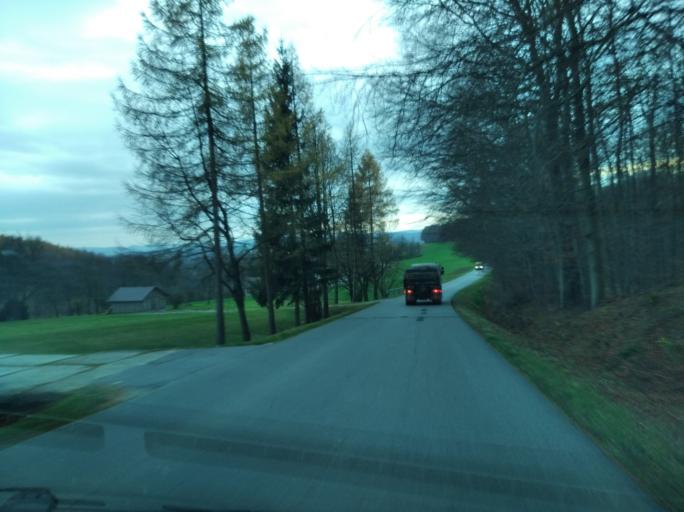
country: PL
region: Subcarpathian Voivodeship
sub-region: Powiat ropczycko-sedziszowski
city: Zagorzyce
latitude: 49.9499
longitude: 21.6963
